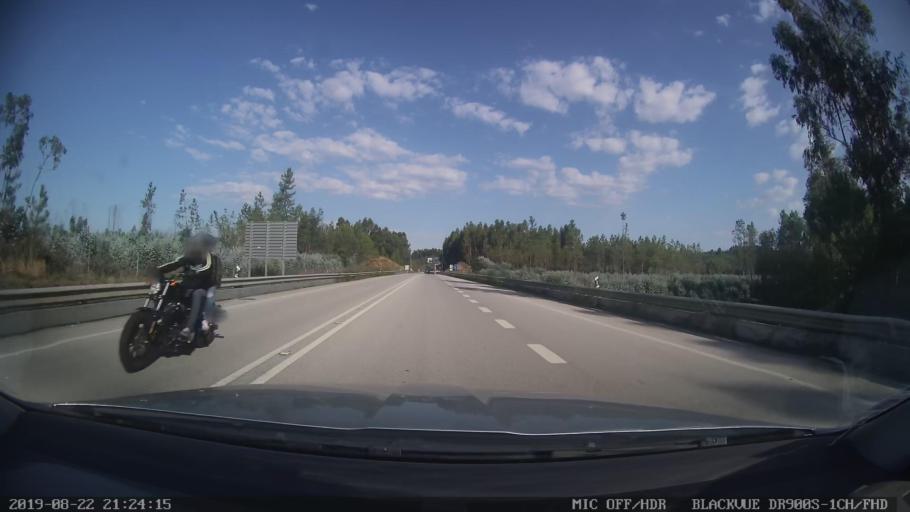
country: PT
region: Castelo Branco
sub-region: Serta
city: Serta
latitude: 39.8394
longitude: -8.1196
